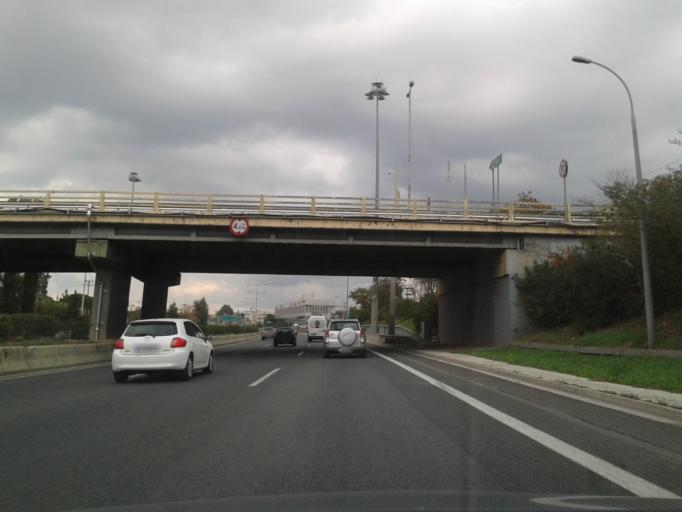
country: GR
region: Attica
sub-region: Nomarchia Athinas
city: Lykovrysi
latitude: 38.0770
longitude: 23.7795
